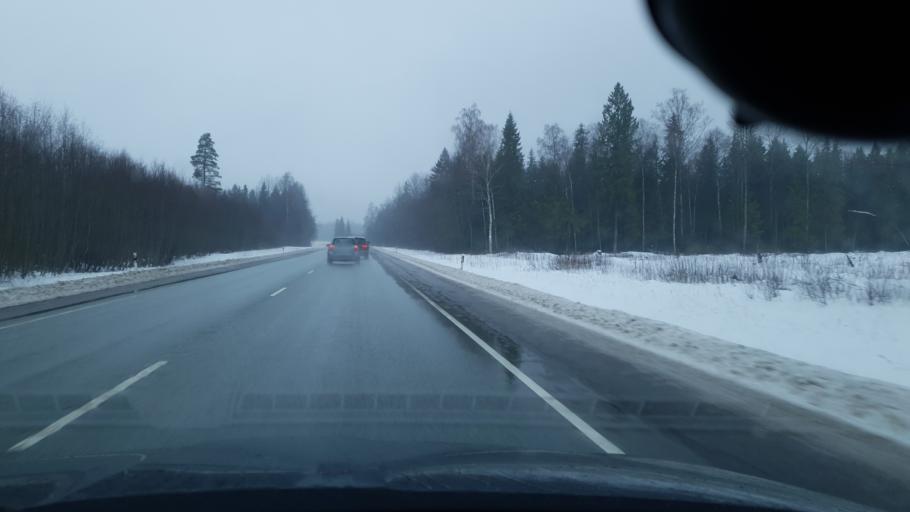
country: EE
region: Jaervamaa
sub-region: Paide linn
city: Paide
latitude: 58.9672
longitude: 25.6046
